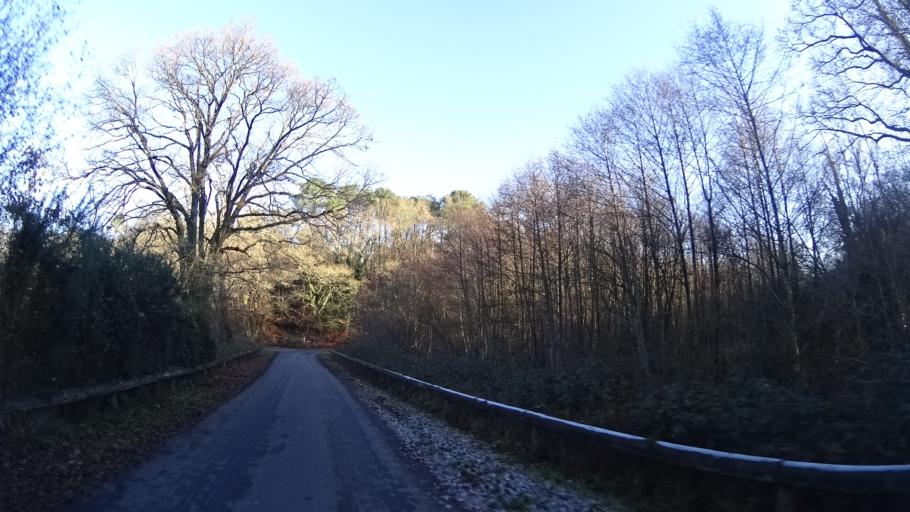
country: FR
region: Brittany
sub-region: Departement du Morbihan
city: Allaire
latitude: 47.6637
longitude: -2.1611
